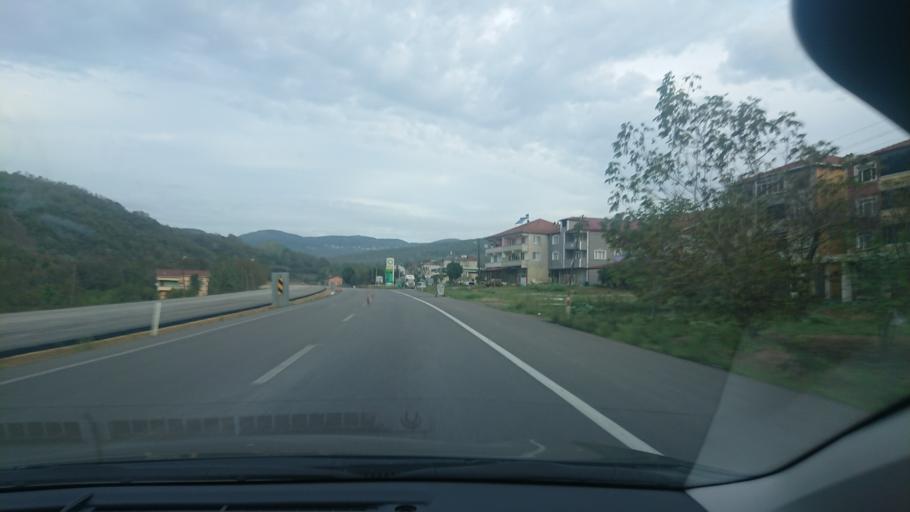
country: TR
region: Zonguldak
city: Beycuma
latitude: 41.3560
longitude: 32.0145
